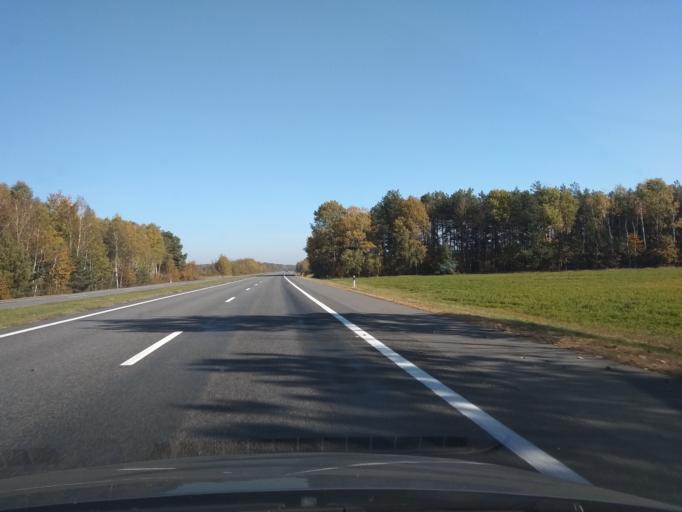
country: BY
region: Brest
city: Antopal'
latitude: 52.3431
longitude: 24.6569
